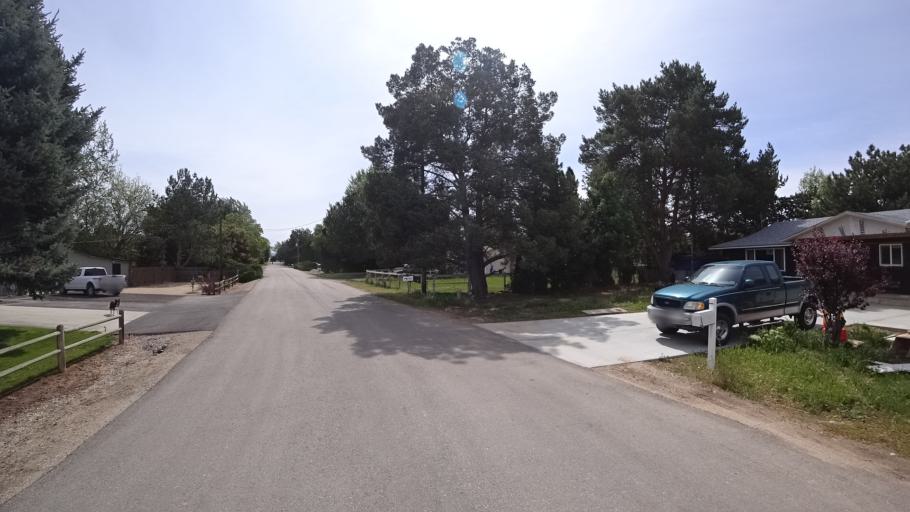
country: US
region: Idaho
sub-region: Ada County
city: Meridian
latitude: 43.5801
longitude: -116.3231
